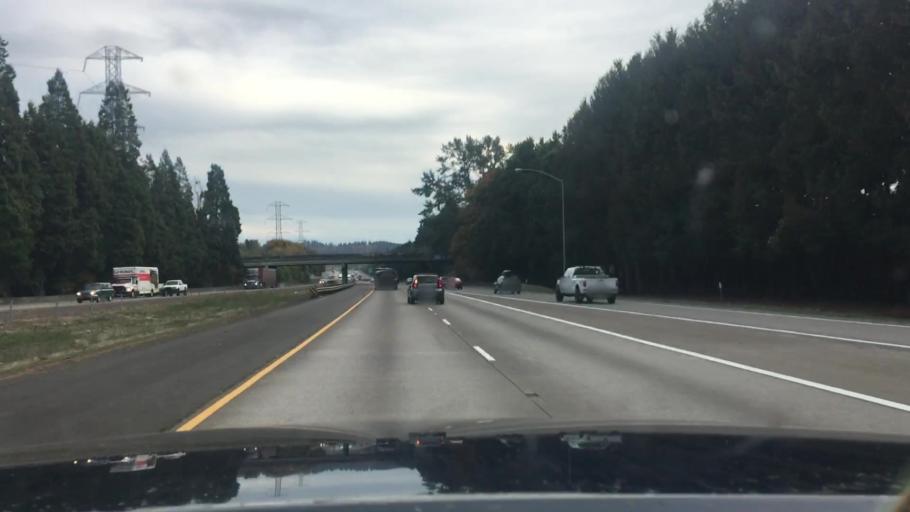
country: US
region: Oregon
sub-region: Lane County
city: Springfield
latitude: 44.0576
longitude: -123.0501
